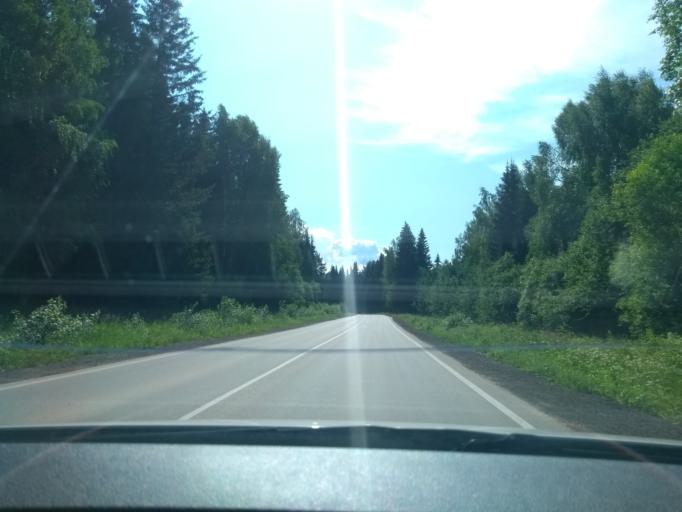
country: RU
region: Perm
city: Bershet'
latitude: 57.8293
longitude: 56.4086
